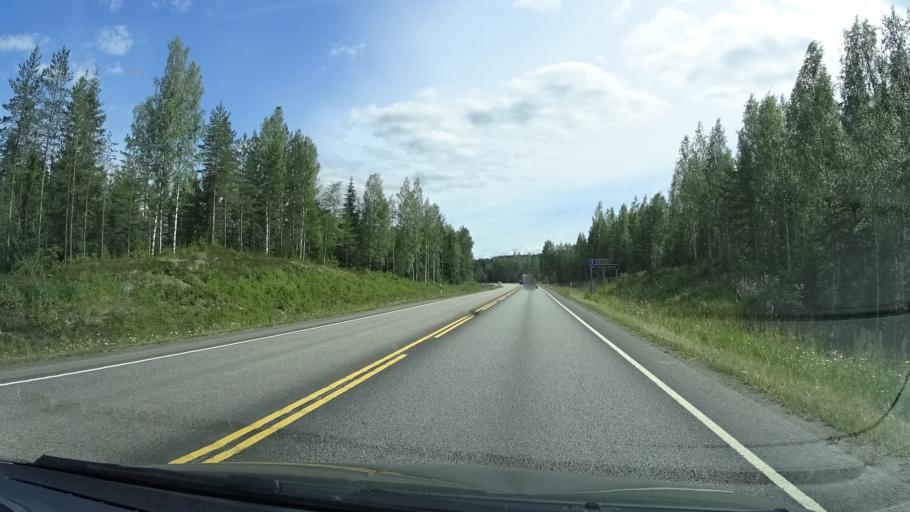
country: FI
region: Central Finland
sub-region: Jyvaeskylae
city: Muurame
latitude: 62.2675
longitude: 25.5173
